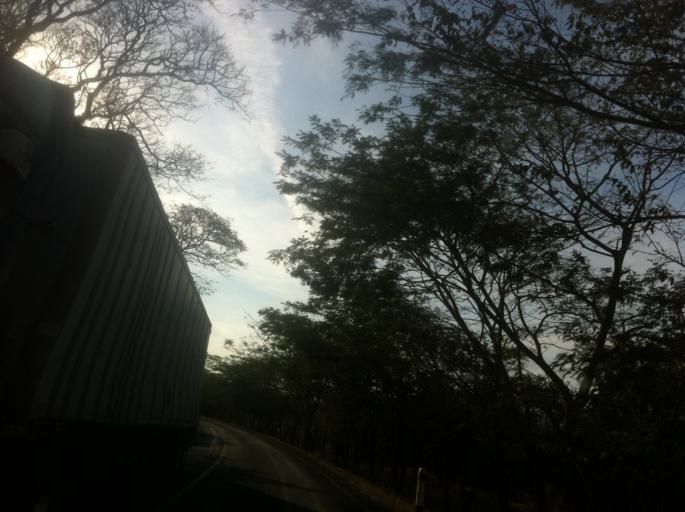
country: NI
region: Rivas
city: Cardenas
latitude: 11.2725
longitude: -85.6517
